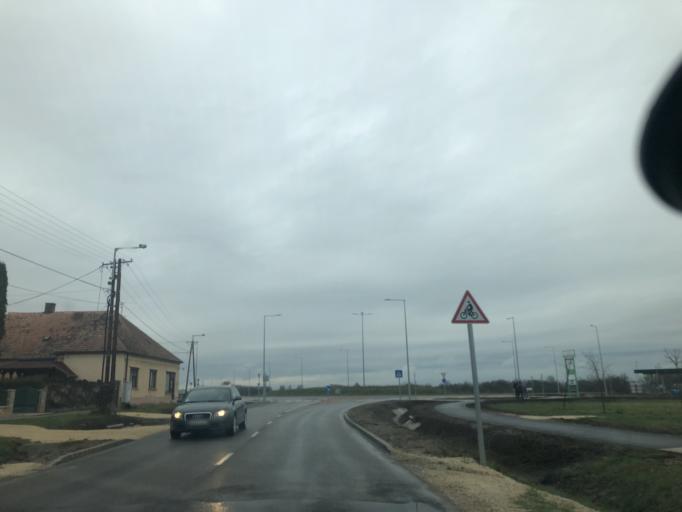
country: HU
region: Gyor-Moson-Sopron
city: Fertod
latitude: 47.6201
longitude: 16.8801
